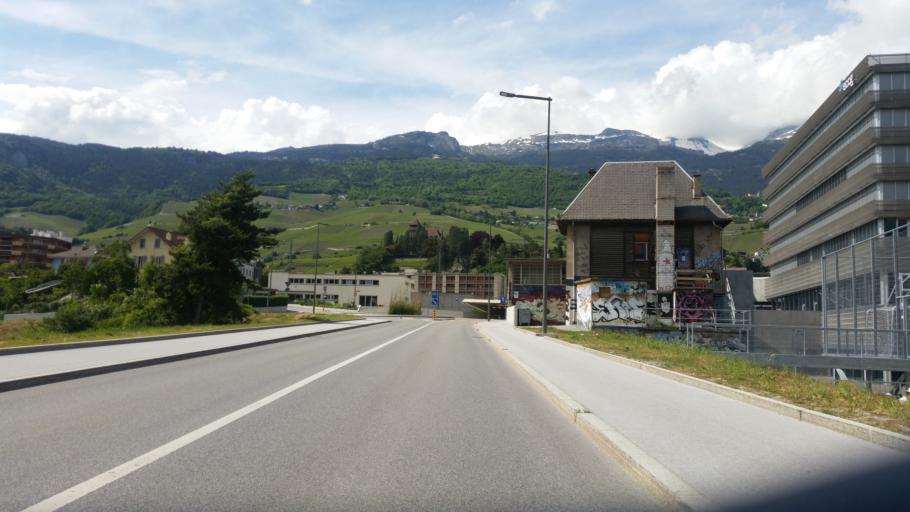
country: CH
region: Valais
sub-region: Sierre District
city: Sierre
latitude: 46.2901
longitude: 7.5324
